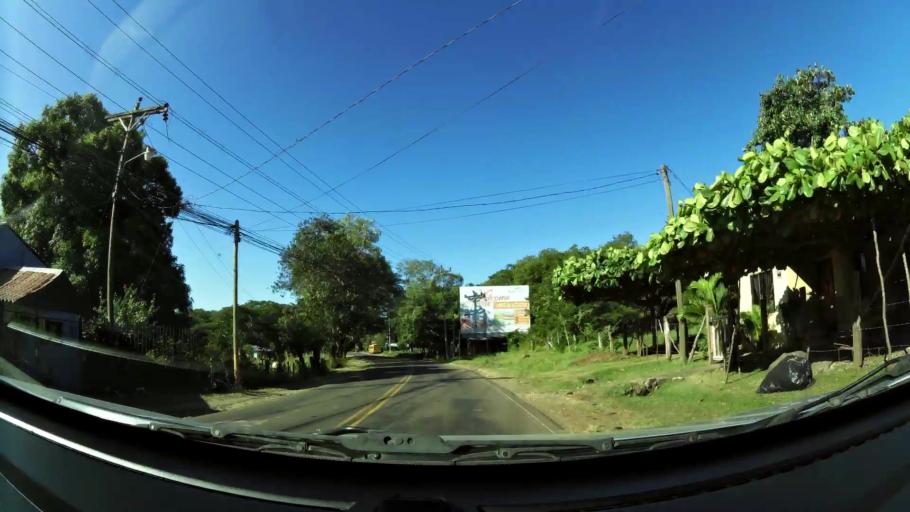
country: CR
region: Guanacaste
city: Belen
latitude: 10.3921
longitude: -85.6163
